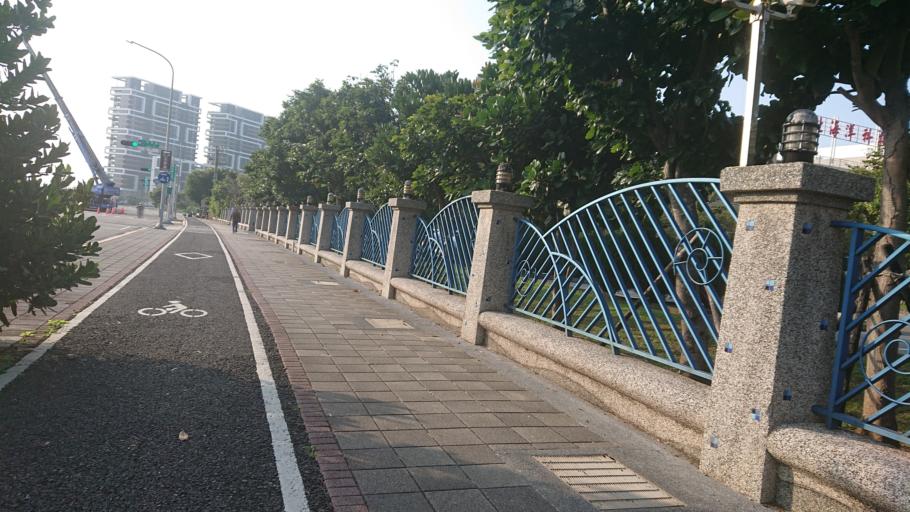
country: TW
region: Taipei
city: Taipei
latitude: 25.1914
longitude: 121.4264
